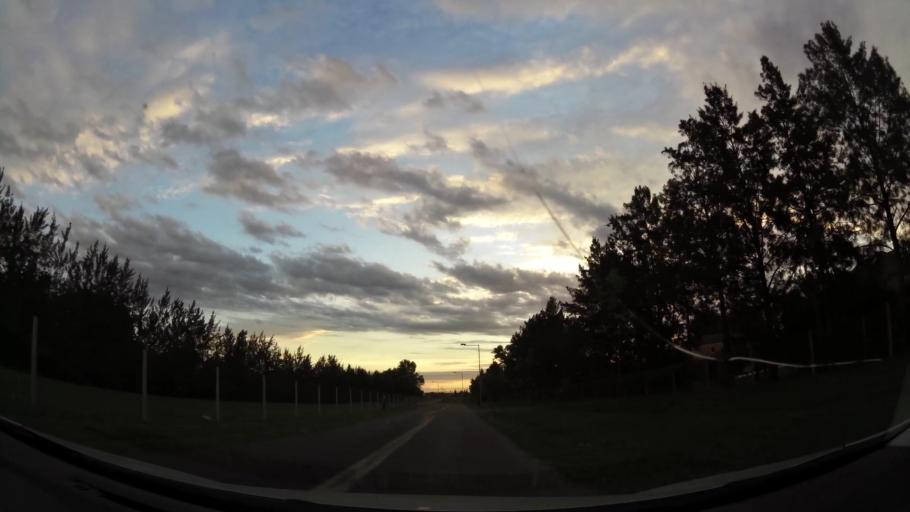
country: AR
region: Buenos Aires
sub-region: Partido de Tigre
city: Tigre
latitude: -34.4416
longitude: -58.6502
